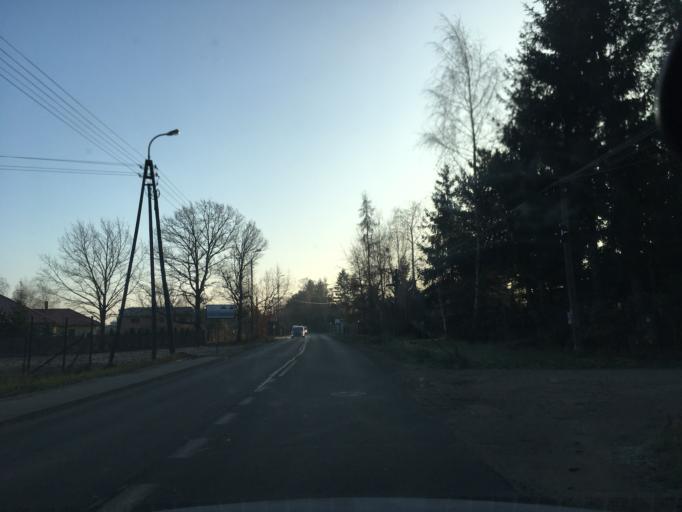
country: PL
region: Masovian Voivodeship
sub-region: Powiat piaseczynski
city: Piaseczno
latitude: 52.0699
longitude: 20.9840
